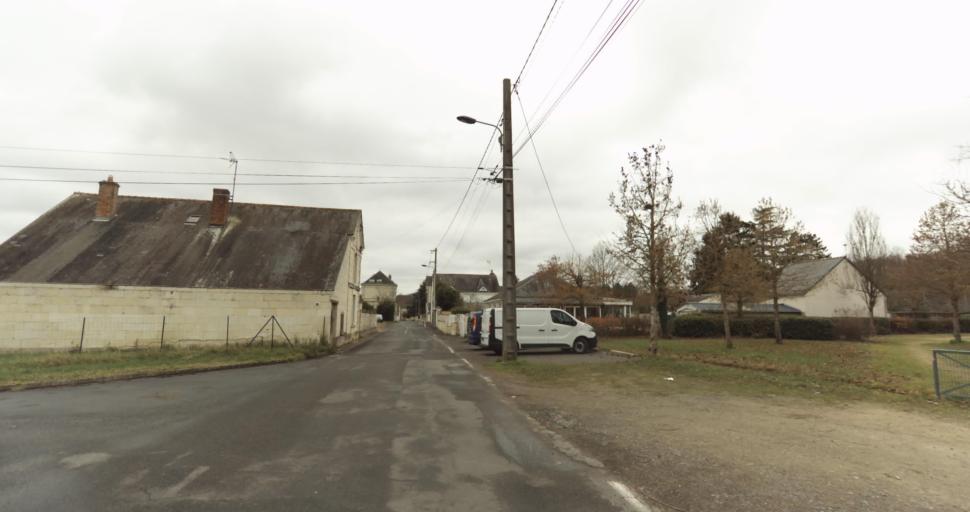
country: FR
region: Pays de la Loire
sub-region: Departement de Maine-et-Loire
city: Distre
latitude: 47.2391
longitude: -0.0939
